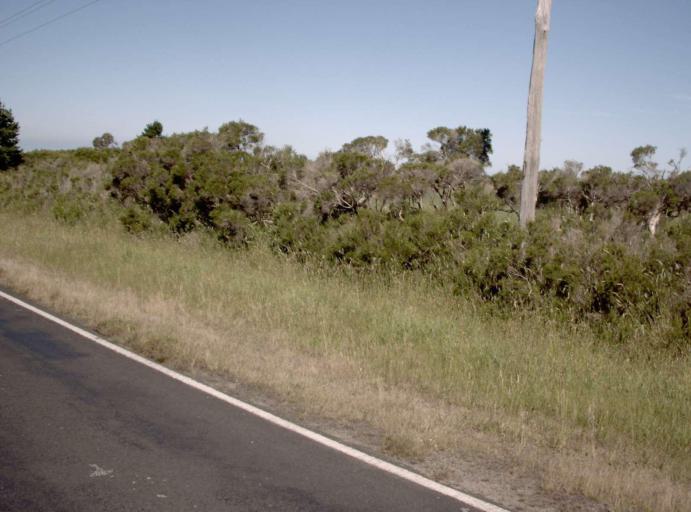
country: AU
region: Victoria
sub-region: Latrobe
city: Traralgon
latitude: -38.6295
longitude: 146.5967
